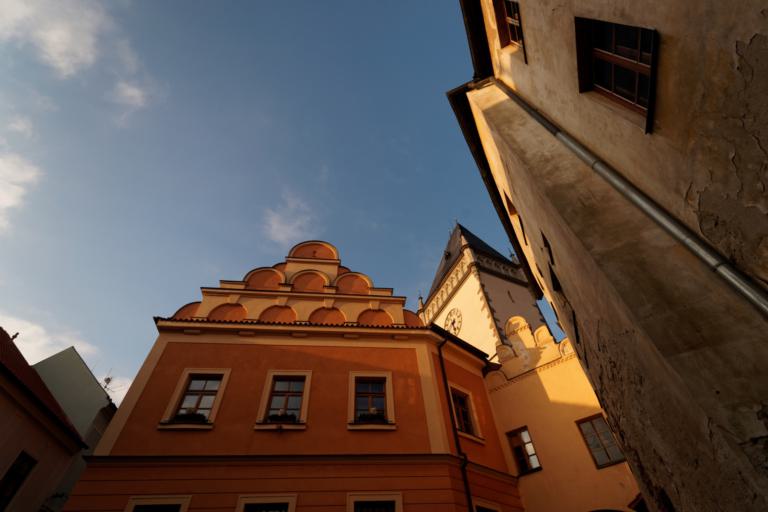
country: CZ
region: Jihocesky
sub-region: Okres Tabor
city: Tabor
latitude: 49.4135
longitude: 14.6575
